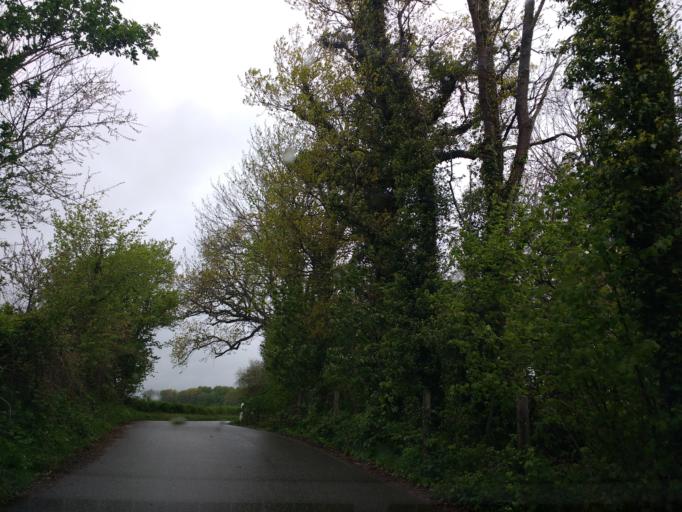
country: DE
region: Schleswig-Holstein
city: Waabs
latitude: 54.5422
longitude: 10.0058
